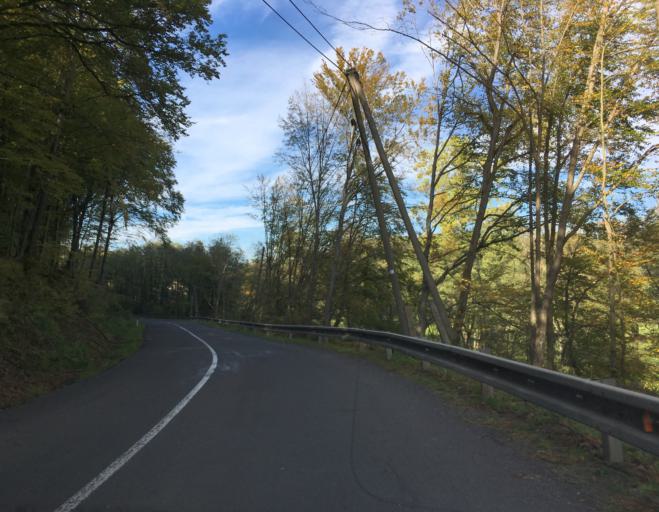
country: SK
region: Banskobystricky
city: Krupina
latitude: 48.3301
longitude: 18.9733
